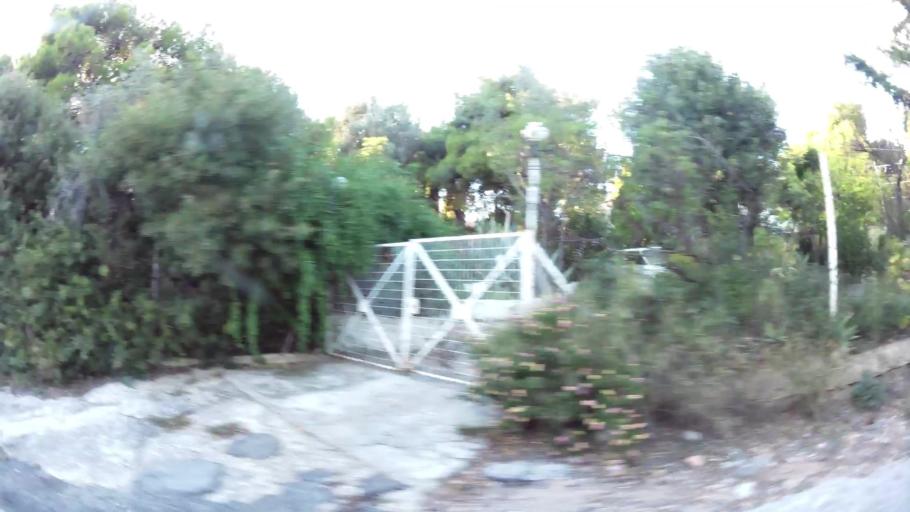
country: GR
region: Attica
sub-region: Nomarchia Athinas
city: Penteli
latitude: 38.0417
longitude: 23.8615
